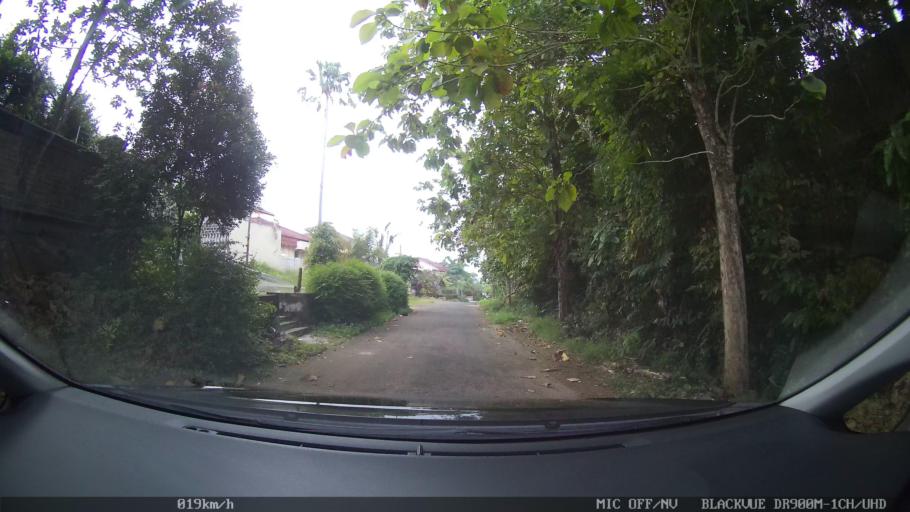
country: ID
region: Lampung
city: Bandarlampung
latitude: -5.4381
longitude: 105.2863
